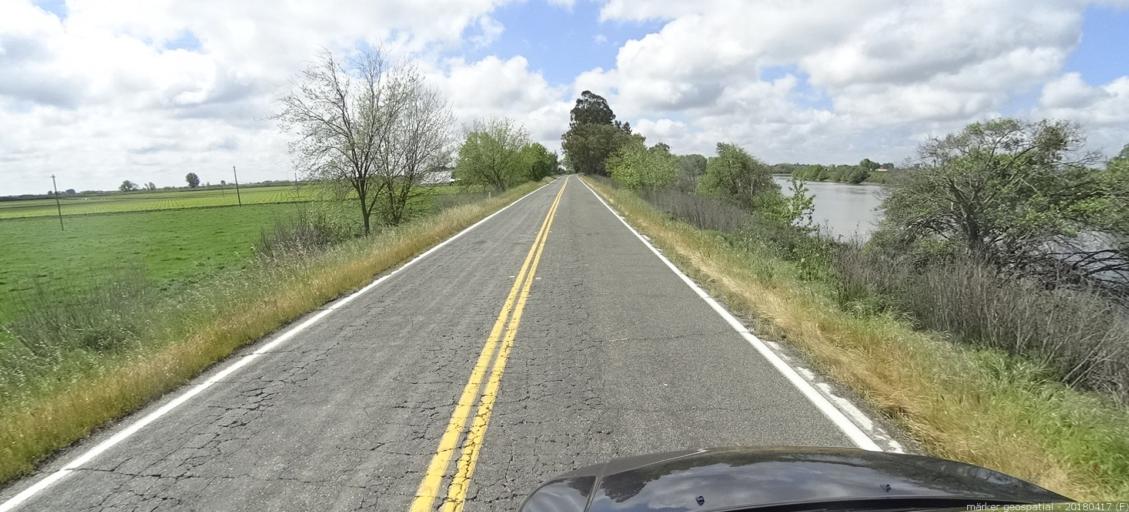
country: US
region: California
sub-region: Sacramento County
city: Walnut Grove
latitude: 38.1987
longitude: -121.5582
